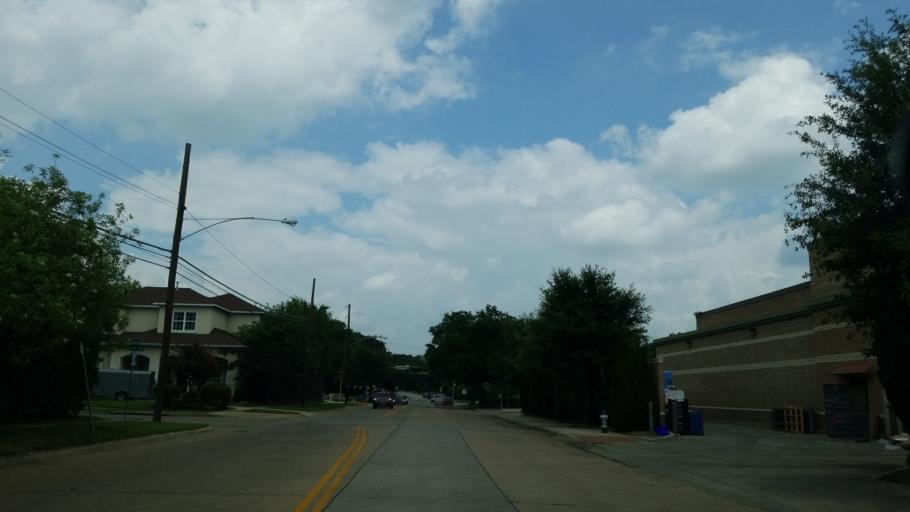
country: US
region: Texas
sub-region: Dallas County
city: University Park
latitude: 32.8449
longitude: -96.8230
